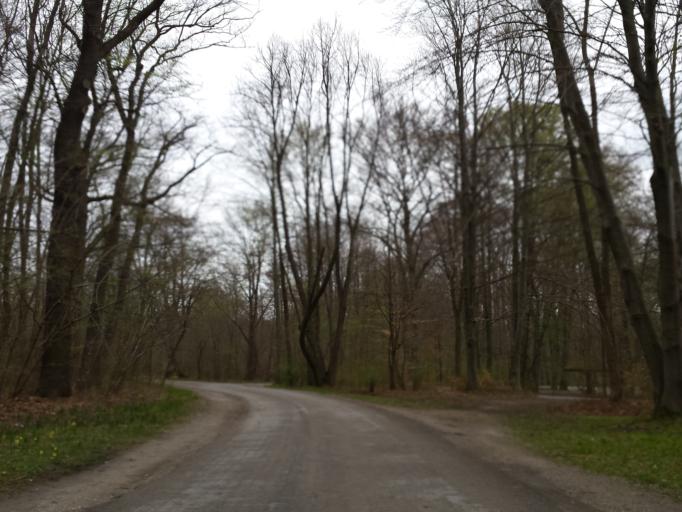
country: DE
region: Bavaria
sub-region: Upper Bavaria
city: Bogenhausen
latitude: 48.1768
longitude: 11.6165
